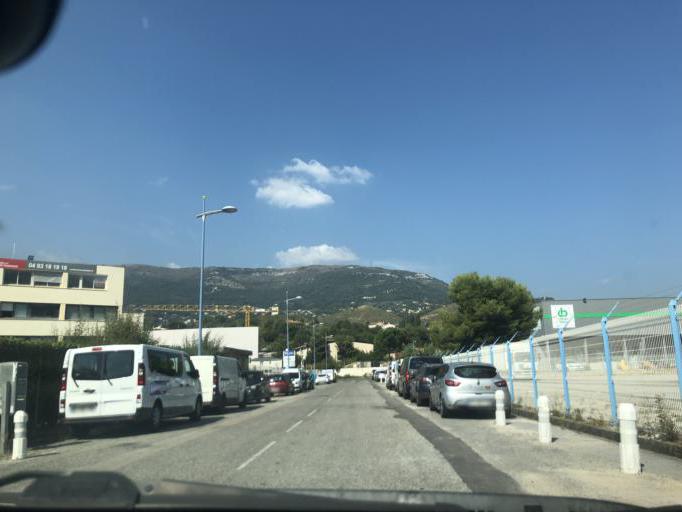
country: FR
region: Provence-Alpes-Cote d'Azur
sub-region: Departement des Alpes-Maritimes
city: Colomars
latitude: 43.7742
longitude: 7.2096
